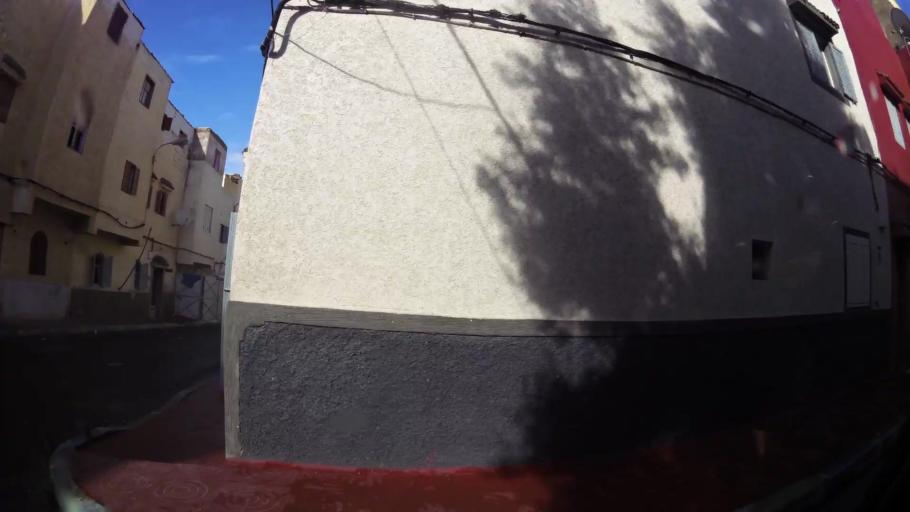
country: MA
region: Grand Casablanca
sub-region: Casablanca
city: Casablanca
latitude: 33.5608
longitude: -7.6946
